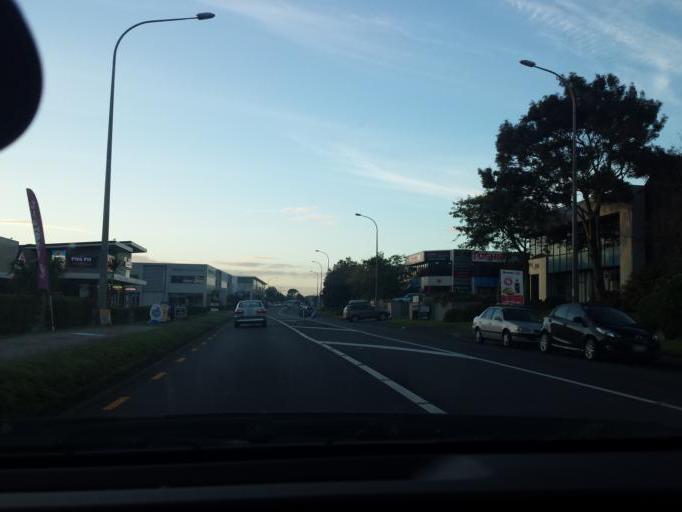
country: NZ
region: Auckland
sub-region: Auckland
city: Tamaki
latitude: -36.8911
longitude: 174.8351
